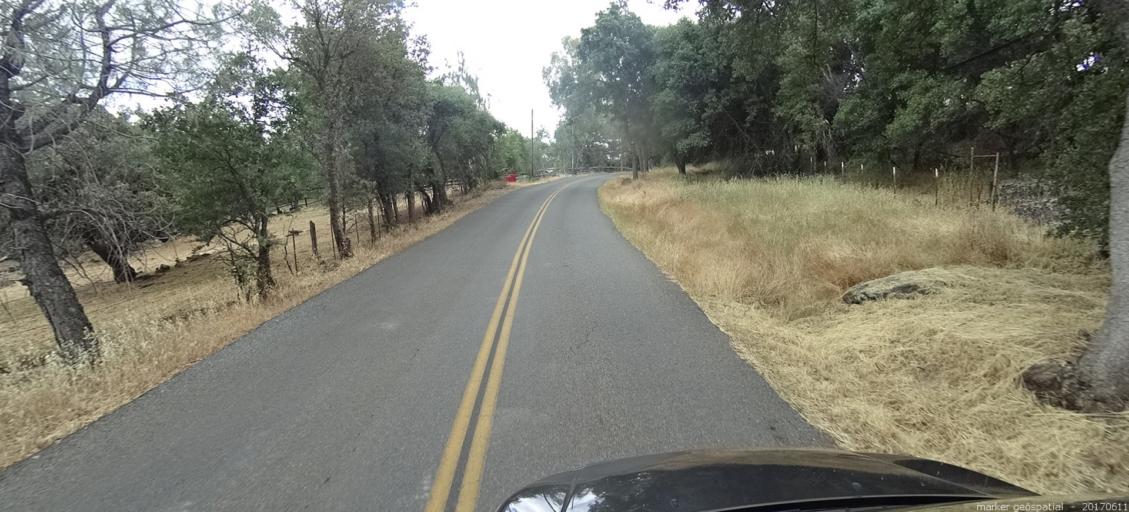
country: US
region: California
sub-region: Butte County
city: Berry Creek
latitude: 39.6356
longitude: -121.5279
